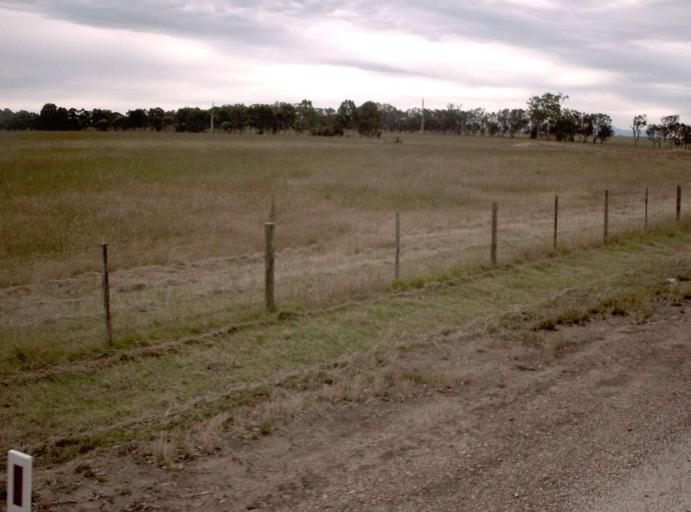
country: AU
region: Victoria
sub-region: Wellington
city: Sale
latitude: -38.0050
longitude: 147.1904
